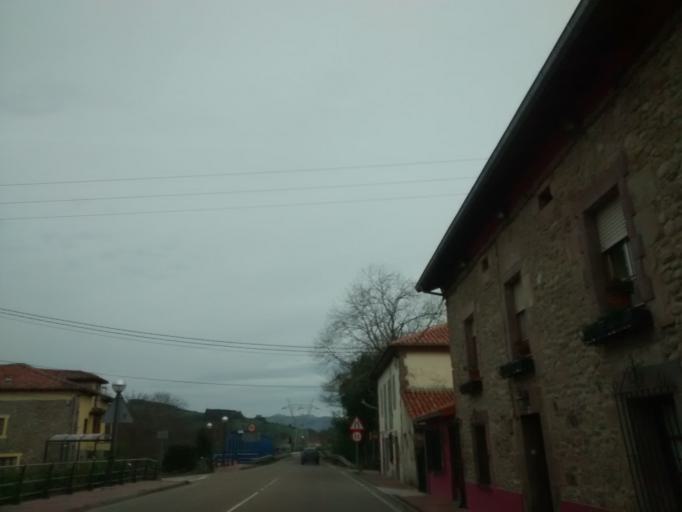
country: ES
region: Cantabria
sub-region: Provincia de Cantabria
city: Puente Viesgo
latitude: 43.3199
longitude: -3.9592
